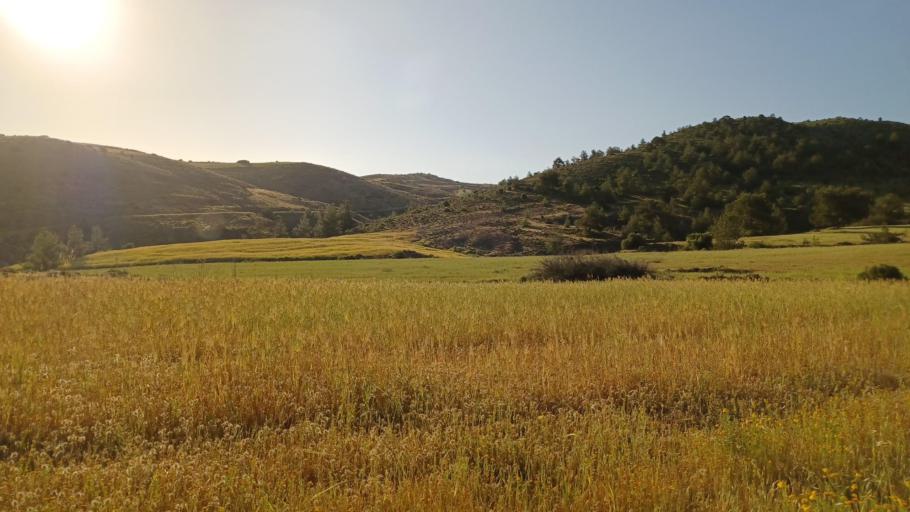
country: CY
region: Lefkosia
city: Peristerona
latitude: 35.0682
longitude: 33.0443
